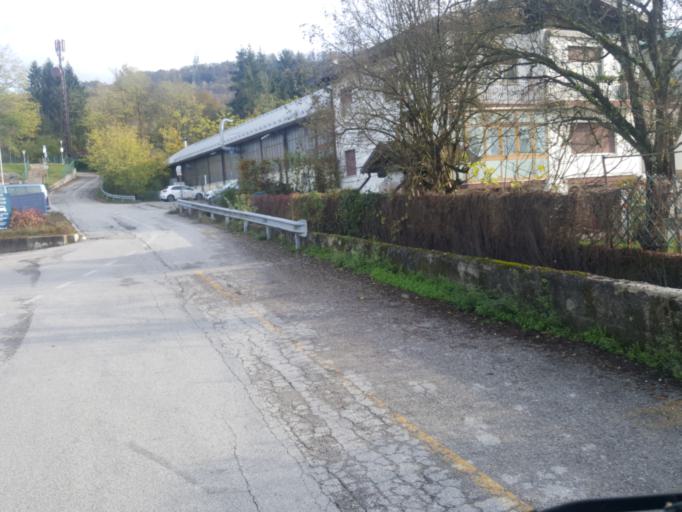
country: IT
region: Veneto
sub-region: Provincia di Belluno
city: Limana
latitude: 46.0947
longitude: 12.1821
